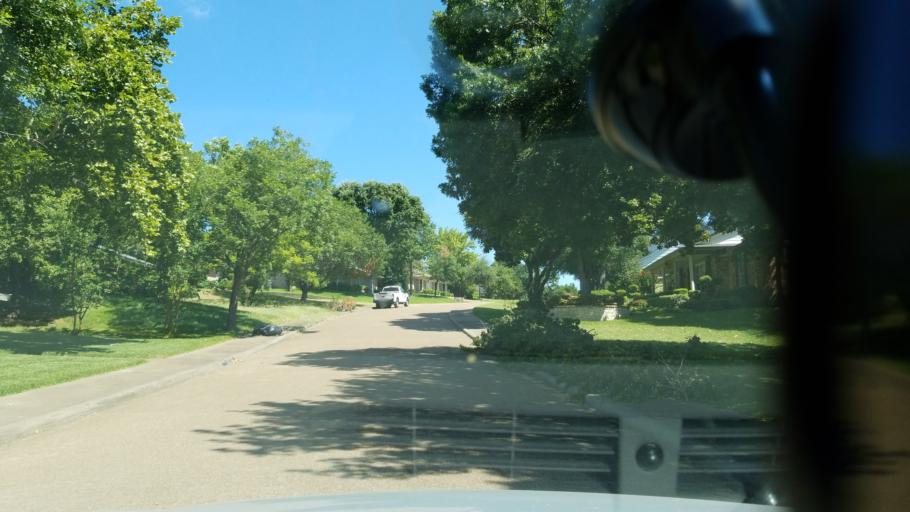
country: US
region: Texas
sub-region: Dallas County
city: Cockrell Hill
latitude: 32.6787
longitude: -96.8334
